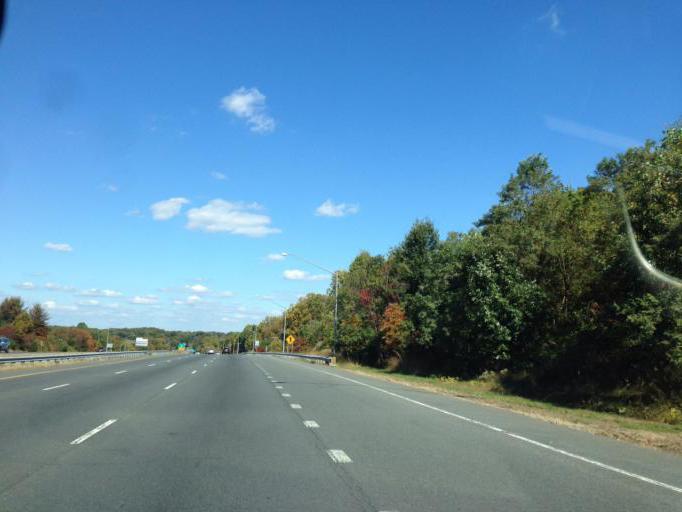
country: US
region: Maryland
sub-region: Howard County
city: Riverside
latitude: 39.1594
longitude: -76.8883
